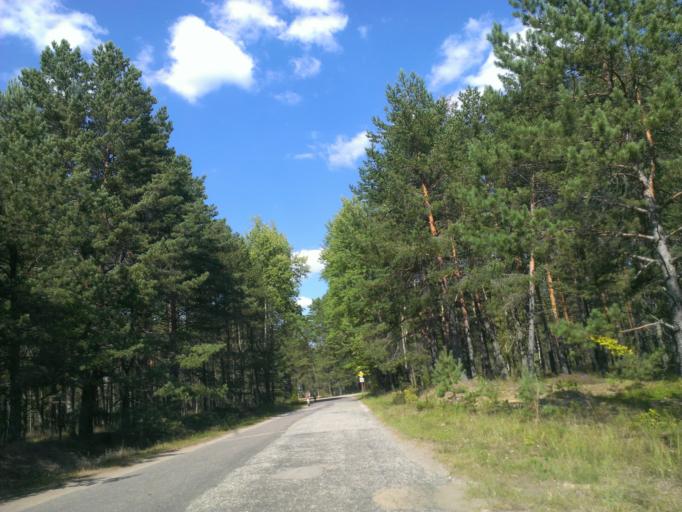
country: LV
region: Adazi
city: Adazi
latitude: 57.1224
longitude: 24.3453
